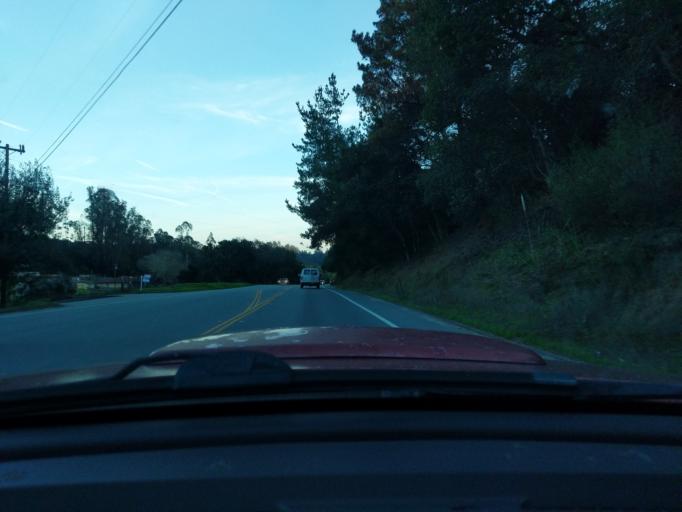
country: US
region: California
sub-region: Monterey County
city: Prunedale
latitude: 36.8075
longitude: -121.6707
